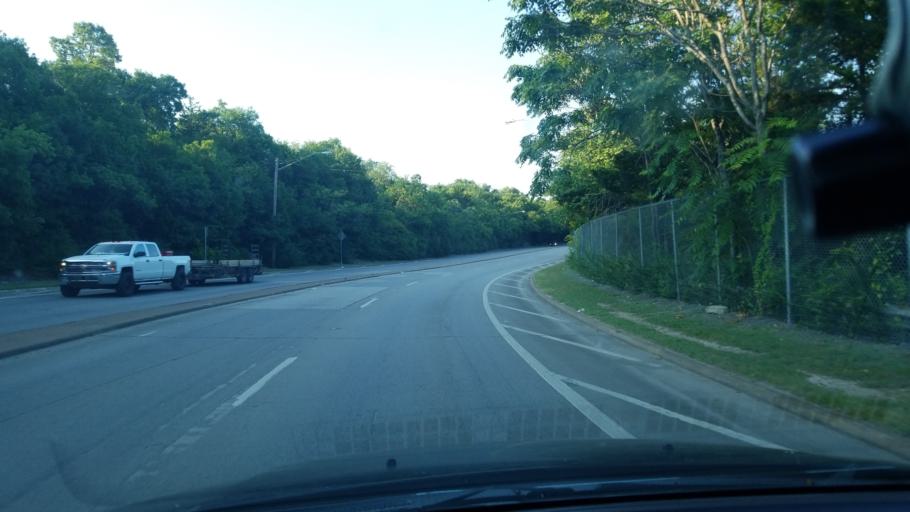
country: US
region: Texas
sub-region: Dallas County
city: Dallas
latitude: 32.7391
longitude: -96.8131
